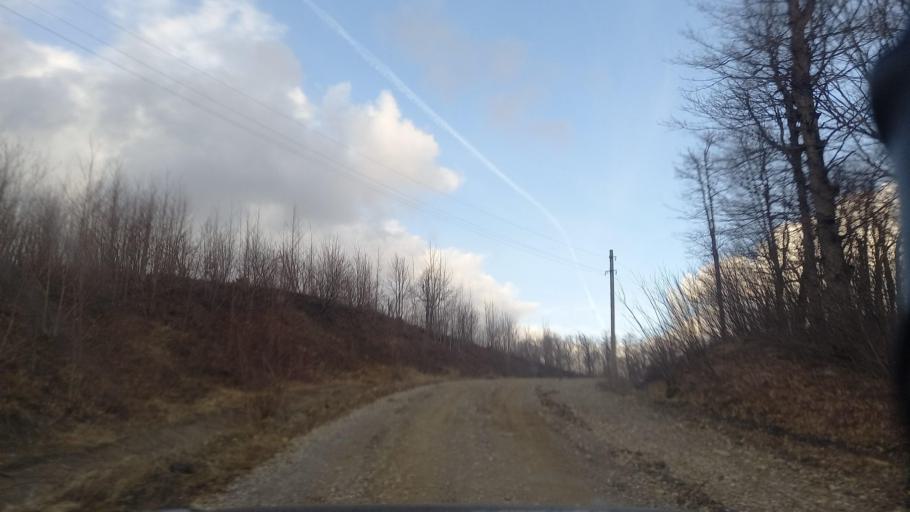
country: RU
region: Krasnodarskiy
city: Dzhubga
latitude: 44.5077
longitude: 38.7708
